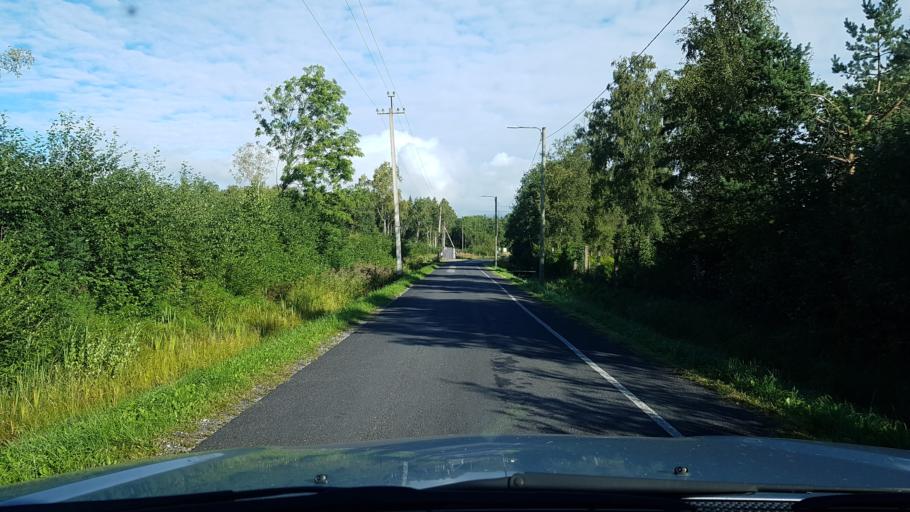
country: EE
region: Harju
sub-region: Rae vald
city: Vaida
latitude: 59.2984
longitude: 24.9169
